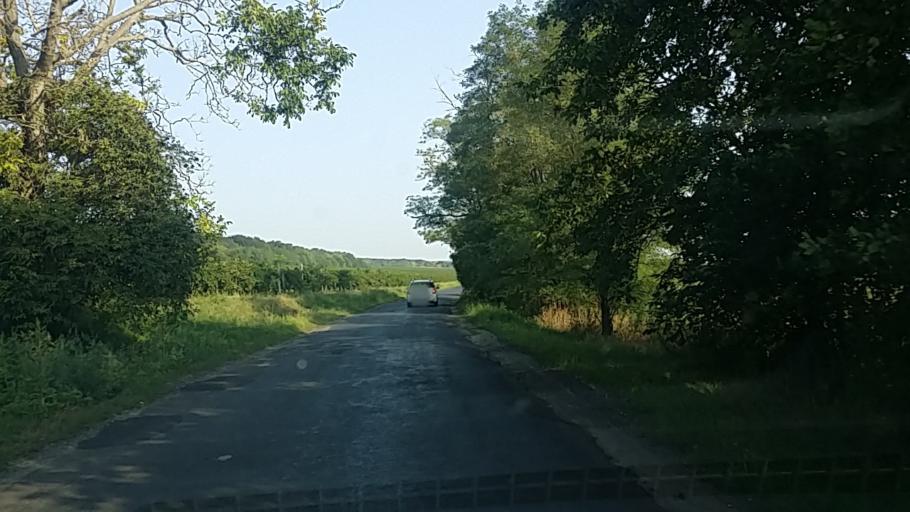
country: HU
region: Gyor-Moson-Sopron
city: Fertorakos
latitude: 47.6954
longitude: 16.6615
